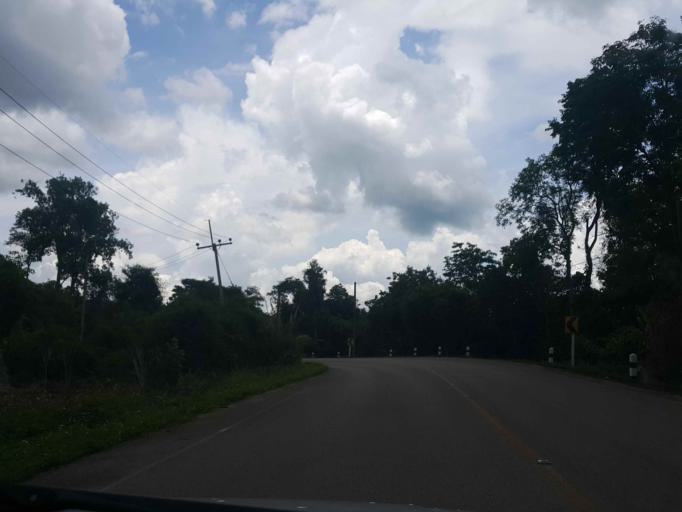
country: TH
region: Lampang
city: Ngao
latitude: 18.9378
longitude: 100.0794
